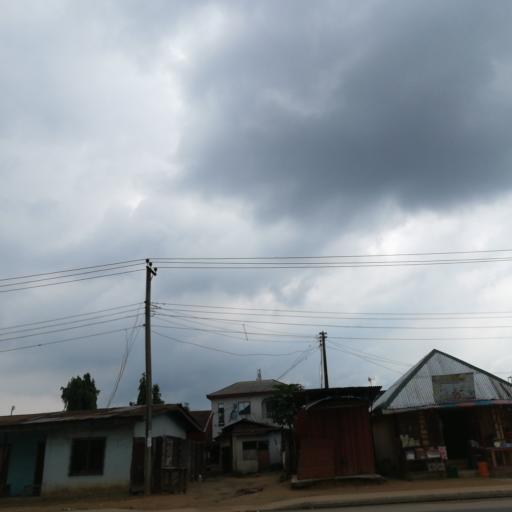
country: NG
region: Rivers
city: Port Harcourt
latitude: 4.8348
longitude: 7.0701
